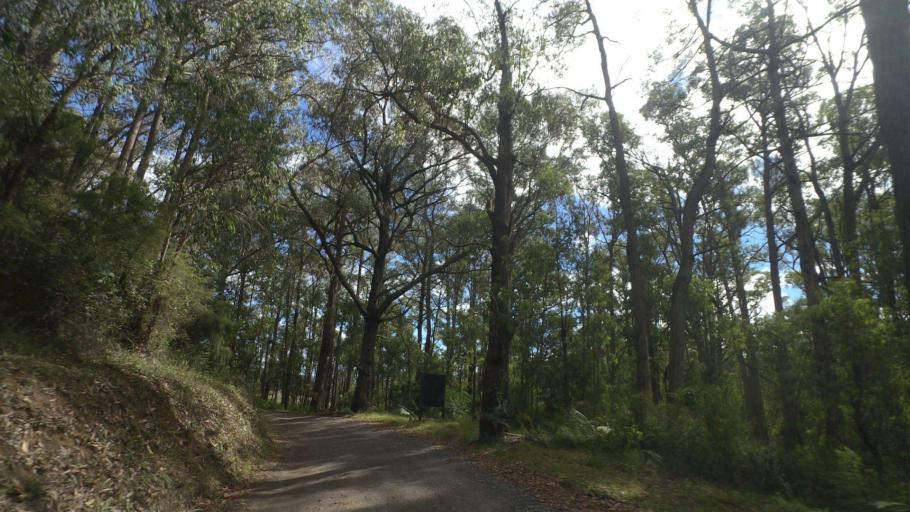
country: AU
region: Victoria
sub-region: Cardinia
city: Gembrook
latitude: -37.8886
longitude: 145.6432
